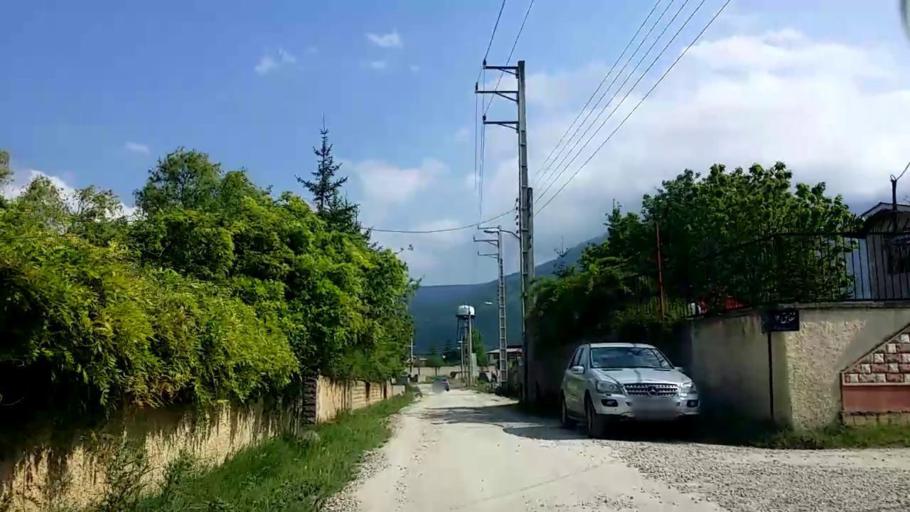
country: IR
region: Mazandaran
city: `Abbasabad
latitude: 36.5228
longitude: 51.1832
